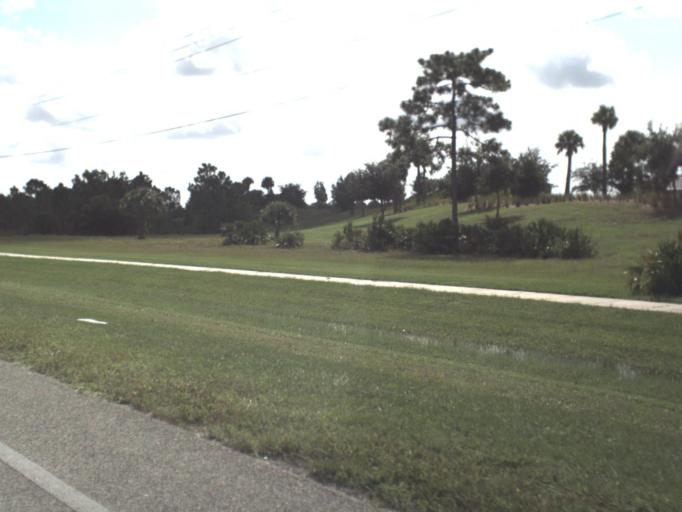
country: US
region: Florida
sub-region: Sarasota County
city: Plantation
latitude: 27.0496
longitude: -82.3752
